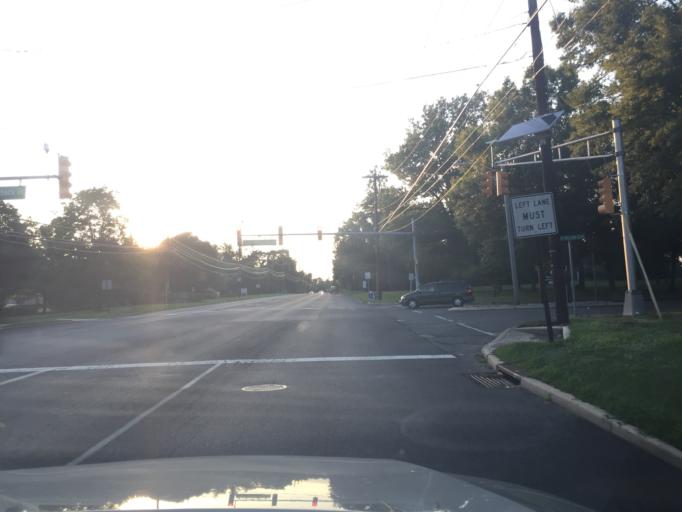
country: US
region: New Jersey
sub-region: Mercer County
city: Princeton Junction
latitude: 40.3003
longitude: -74.6052
